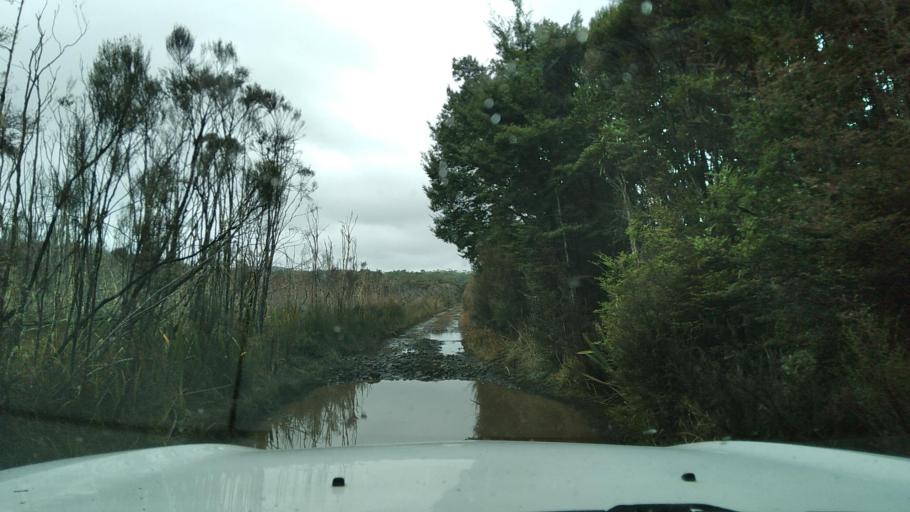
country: NZ
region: Manawatu-Wanganui
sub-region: Ruapehu District
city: Waiouru
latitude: -39.4110
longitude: 175.4885
